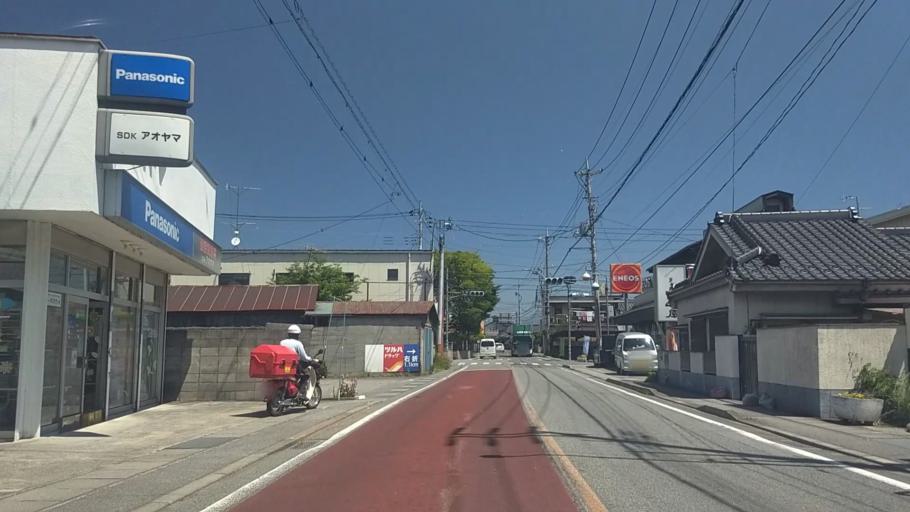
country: JP
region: Yamanashi
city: Ryuo
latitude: 35.6619
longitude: 138.4650
